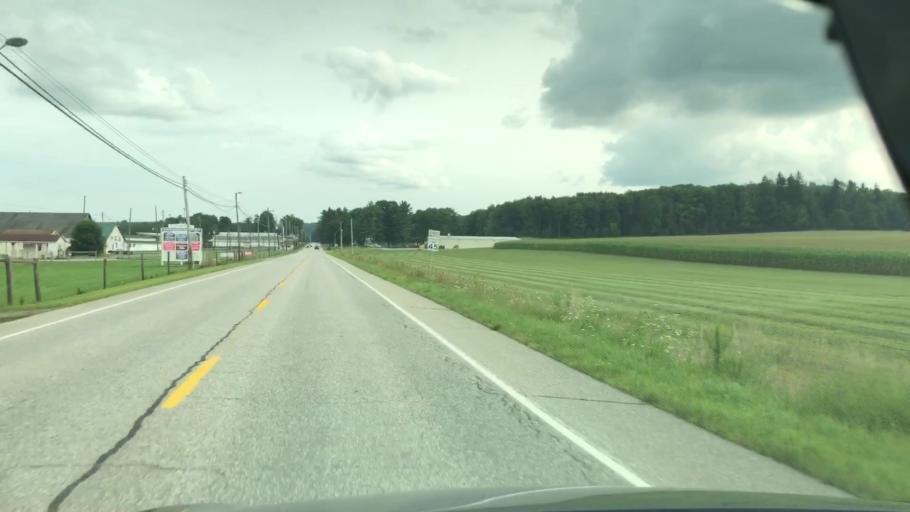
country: US
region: Pennsylvania
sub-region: Erie County
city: Union City
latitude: 42.0168
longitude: -79.8165
